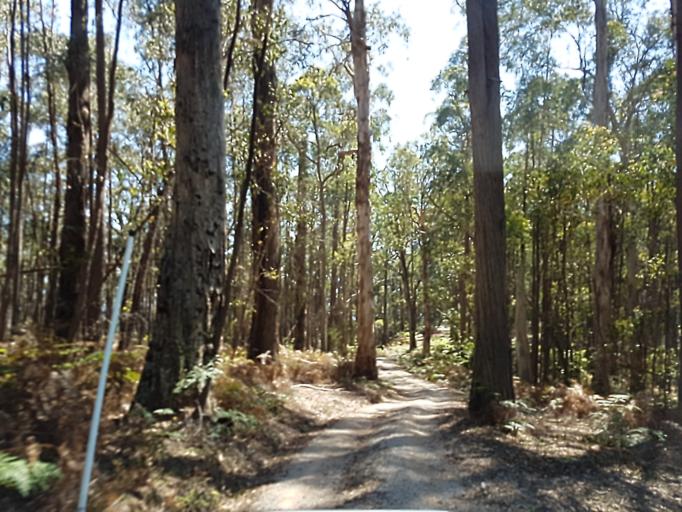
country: AU
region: Victoria
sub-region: East Gippsland
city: Lakes Entrance
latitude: -37.2912
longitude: 148.3203
